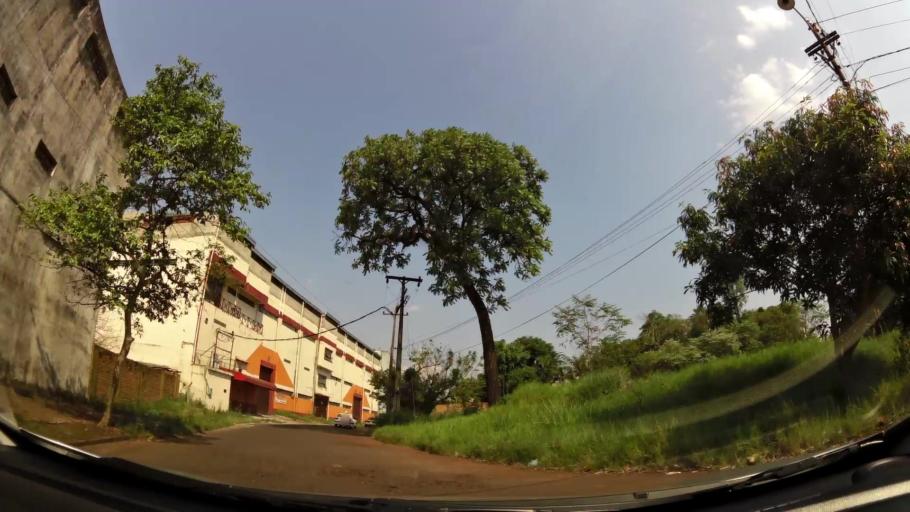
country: PY
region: Alto Parana
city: Ciudad del Este
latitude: -25.5059
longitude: -54.6226
